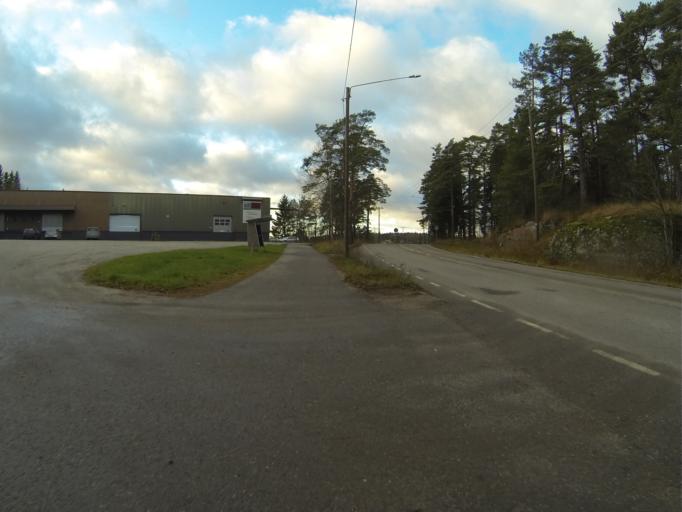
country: FI
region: Varsinais-Suomi
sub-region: Salo
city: Halikko
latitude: 60.3983
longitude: 23.0575
